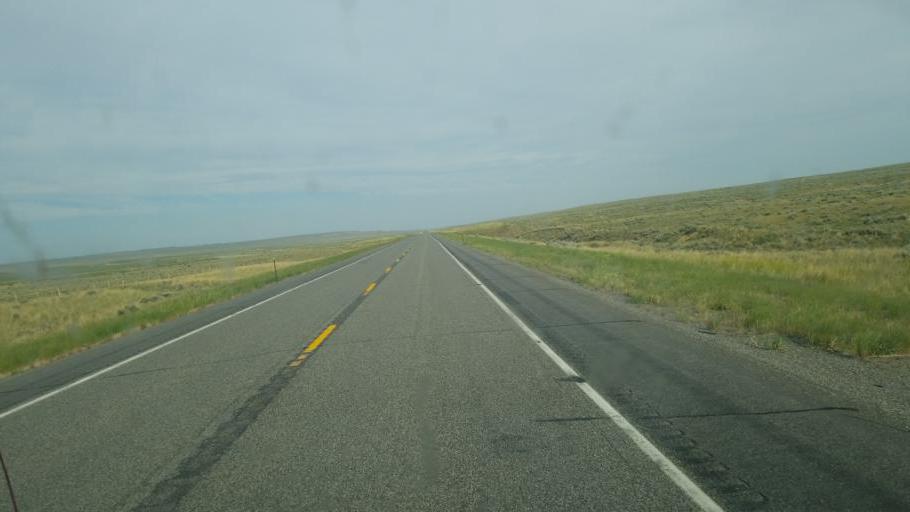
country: US
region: Wyoming
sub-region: Fremont County
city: Riverton
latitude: 43.1757
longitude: -107.8475
